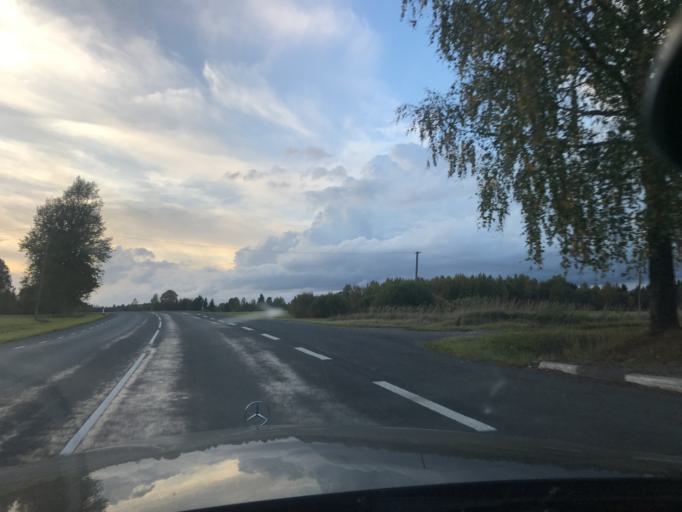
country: EE
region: Vorumaa
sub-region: Antsla vald
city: Vana-Antsla
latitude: 57.9114
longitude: 26.4088
